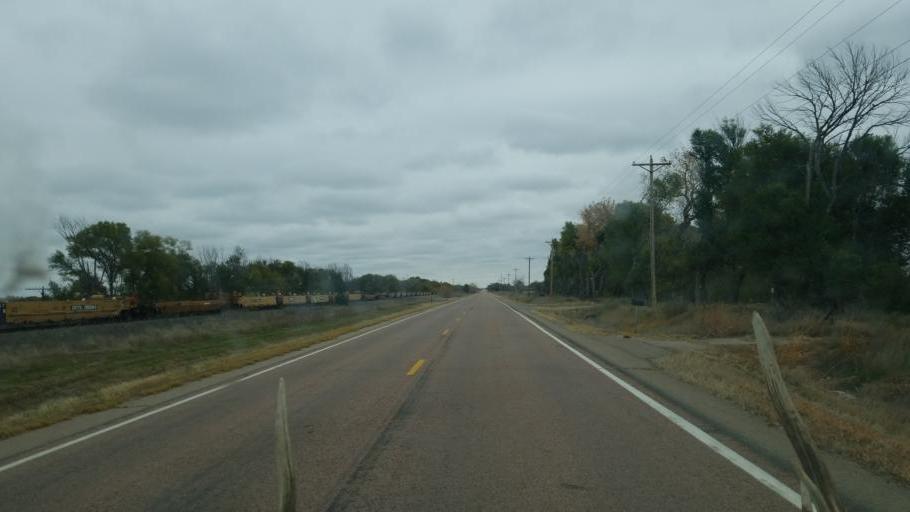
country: US
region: Colorado
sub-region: Otero County
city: Fowler
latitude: 38.1769
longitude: -103.9083
